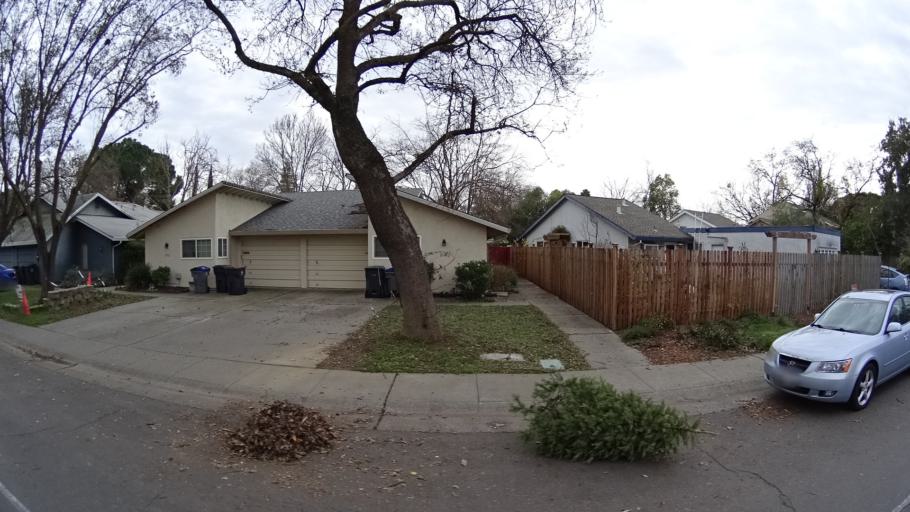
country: US
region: California
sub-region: Yolo County
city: Davis
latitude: 38.5539
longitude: -121.7251
